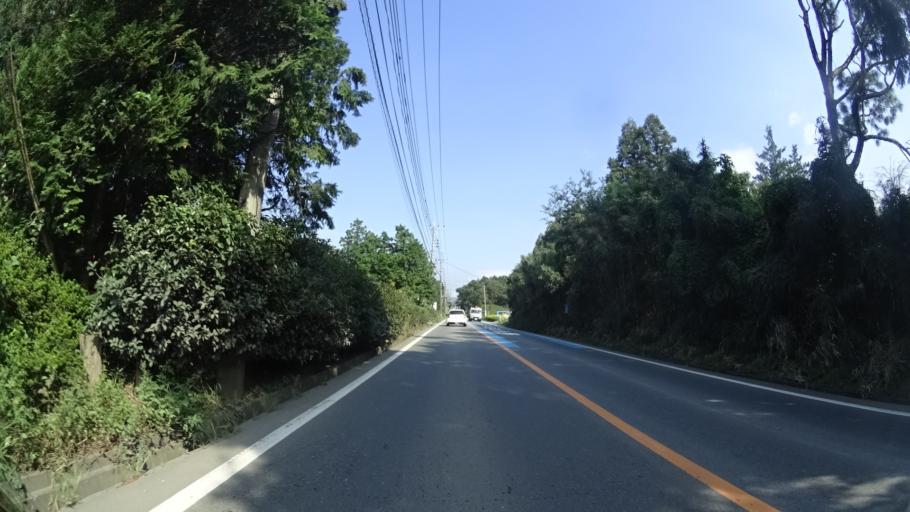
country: JP
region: Kumamoto
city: Ozu
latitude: 32.8881
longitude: 130.8981
